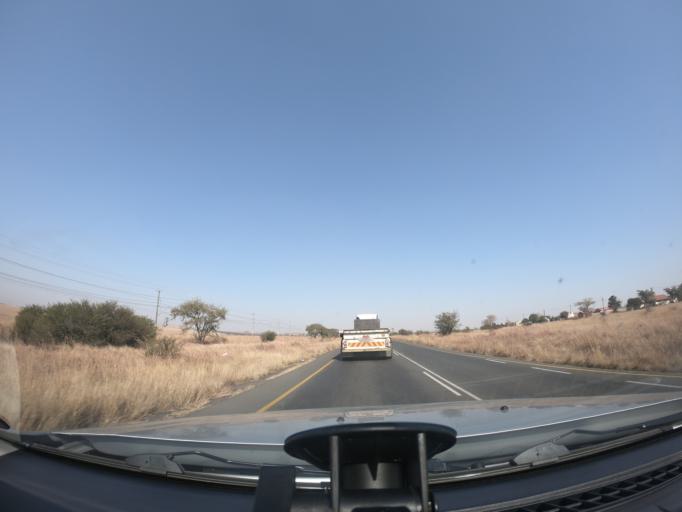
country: ZA
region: KwaZulu-Natal
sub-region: uThukela District Municipality
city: Ladysmith
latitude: -28.7559
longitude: 29.8220
